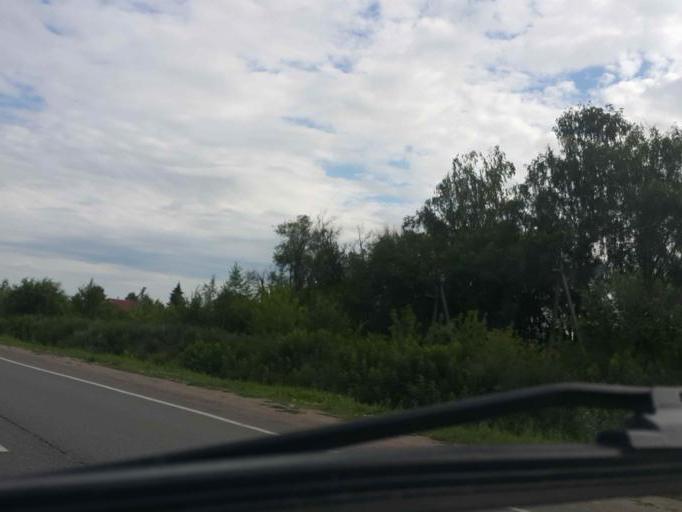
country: RU
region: Tambov
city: Bokino
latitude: 52.6264
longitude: 41.4439
